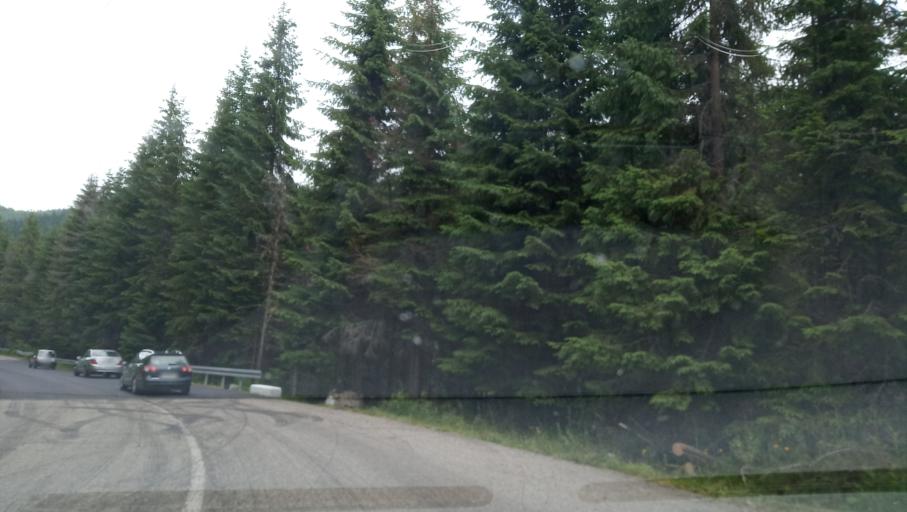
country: RO
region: Gorj
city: Novaci-Straini
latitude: 45.4296
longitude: 23.6787
